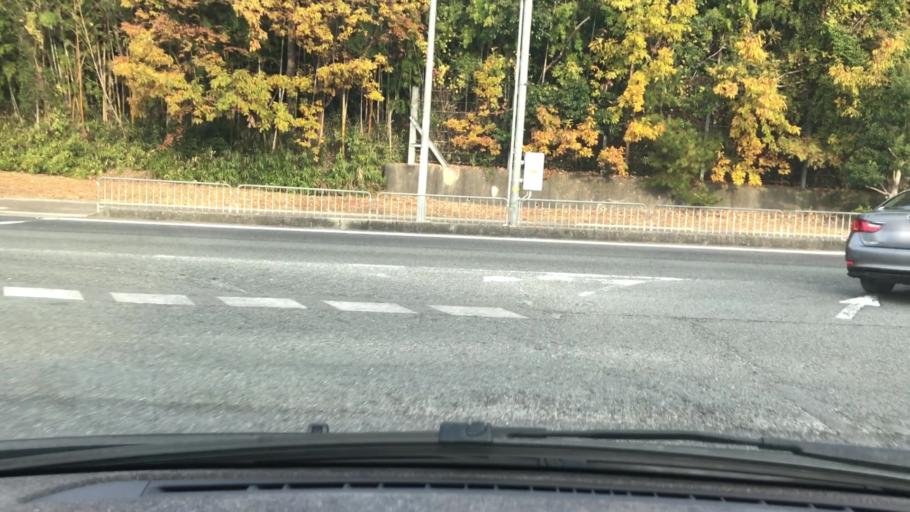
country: JP
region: Hyogo
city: Sandacho
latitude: 34.8286
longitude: 135.2494
